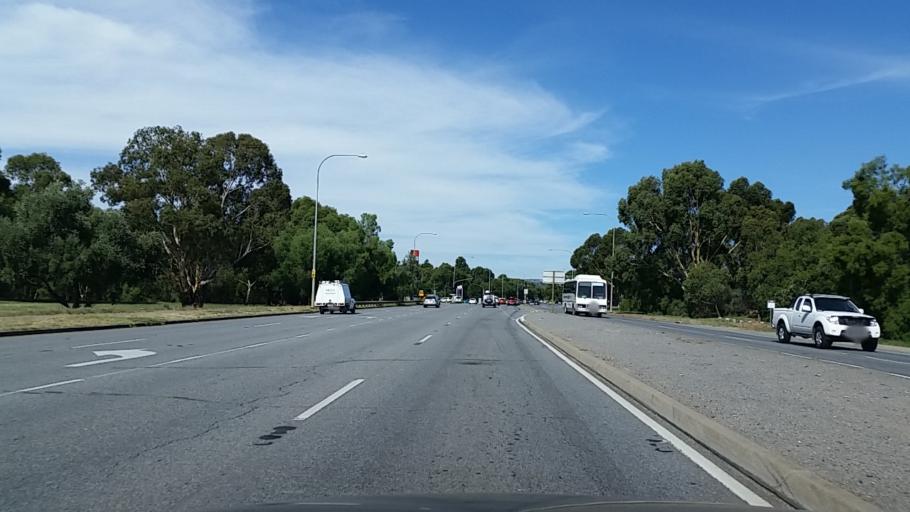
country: AU
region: South Australia
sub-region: Salisbury
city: Ingle Farm
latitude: -34.8248
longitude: 138.6153
